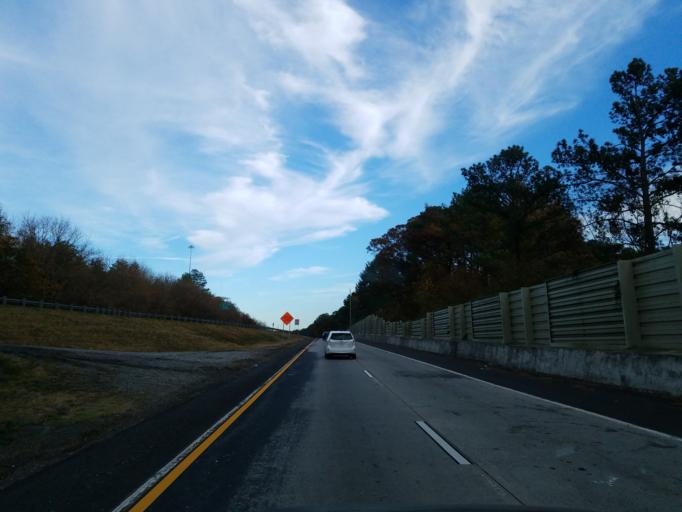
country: US
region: Georgia
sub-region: Fulton County
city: East Point
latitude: 33.7607
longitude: -84.4875
